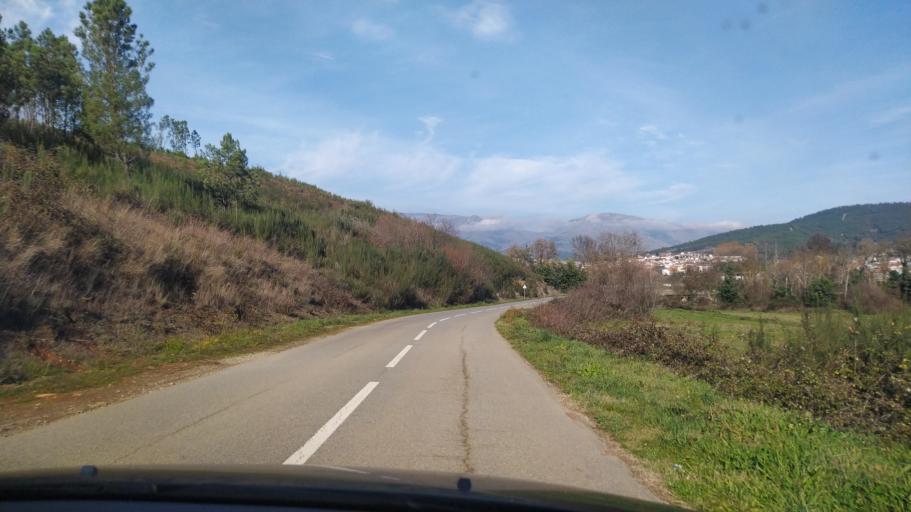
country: PT
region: Castelo Branco
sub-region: Concelho do Fundao
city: Aldeia de Joanes
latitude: 40.1867
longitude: -7.6436
